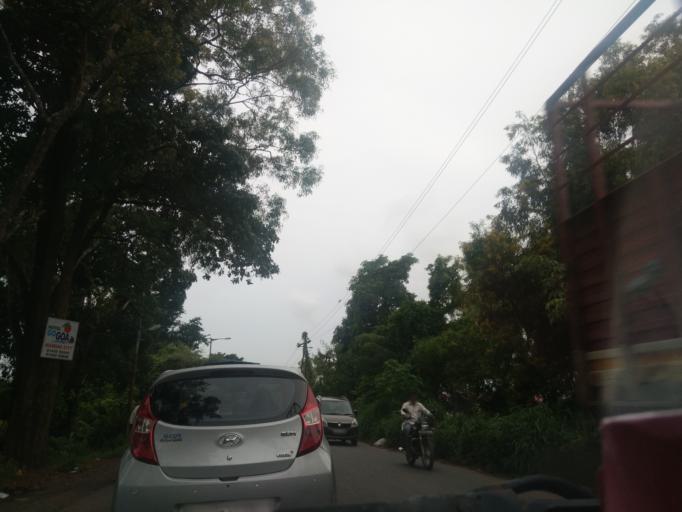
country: IN
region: Goa
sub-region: South Goa
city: Davorlim
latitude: 15.2686
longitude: 73.9778
